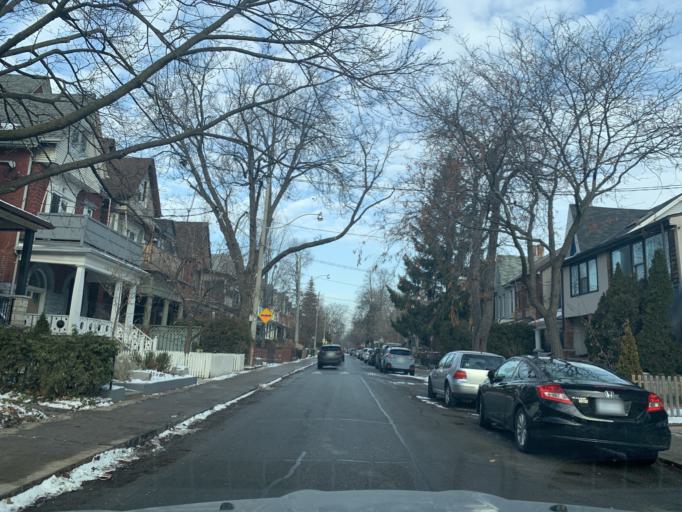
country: CA
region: Ontario
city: Toronto
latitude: 43.6594
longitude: -79.4036
